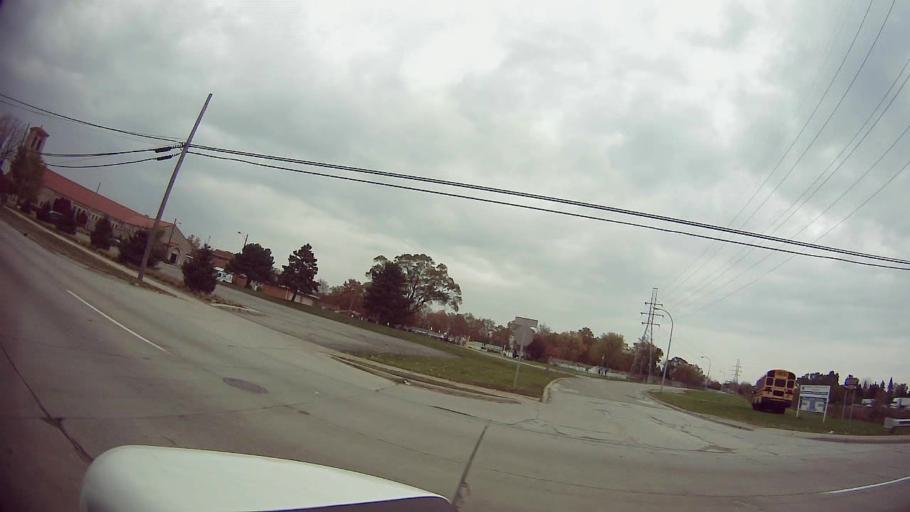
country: US
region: Michigan
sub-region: Macomb County
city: Center Line
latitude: 42.5294
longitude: -83.0475
